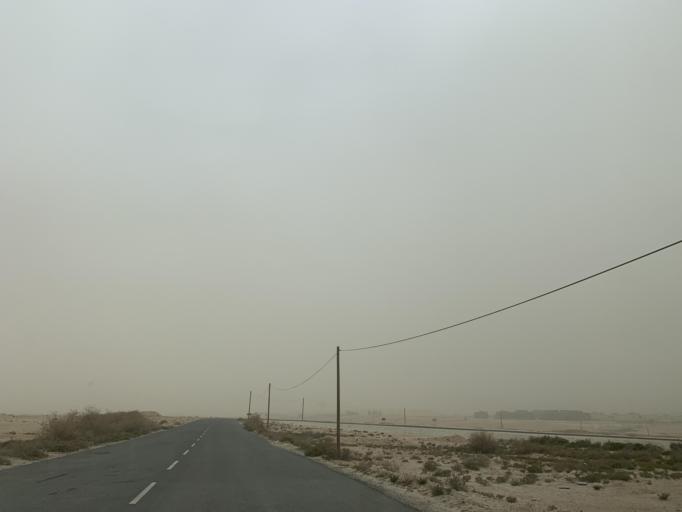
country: BH
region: Central Governorate
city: Madinat Hamad
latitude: 26.1296
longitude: 50.5194
